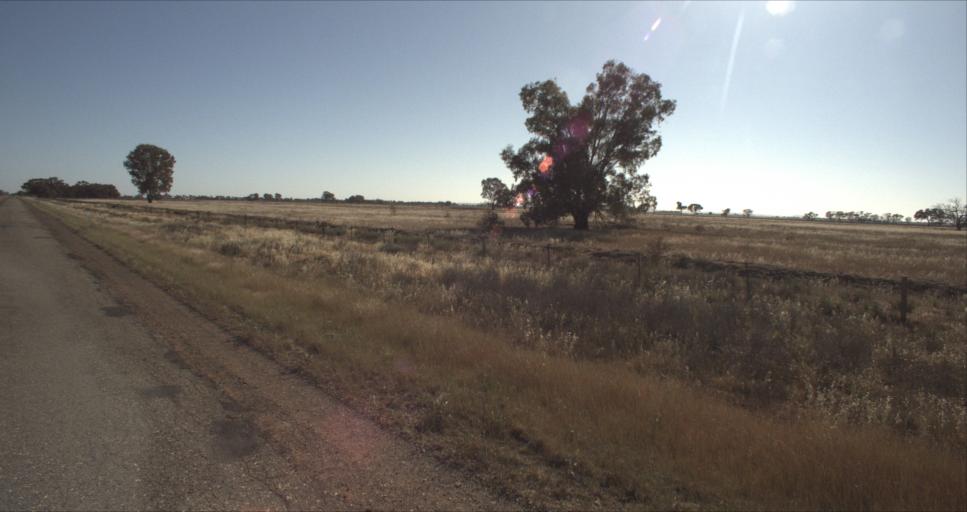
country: AU
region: New South Wales
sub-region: Leeton
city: Leeton
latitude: -34.5961
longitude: 146.2586
